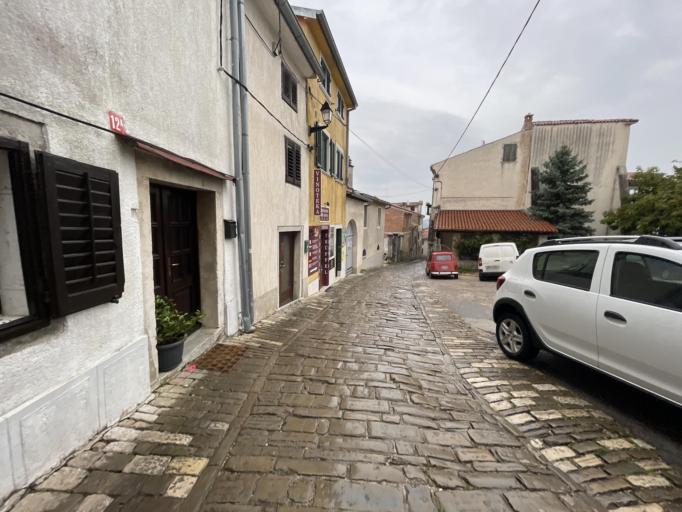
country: HR
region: Istarska
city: Karojba
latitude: 45.3375
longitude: 13.8296
